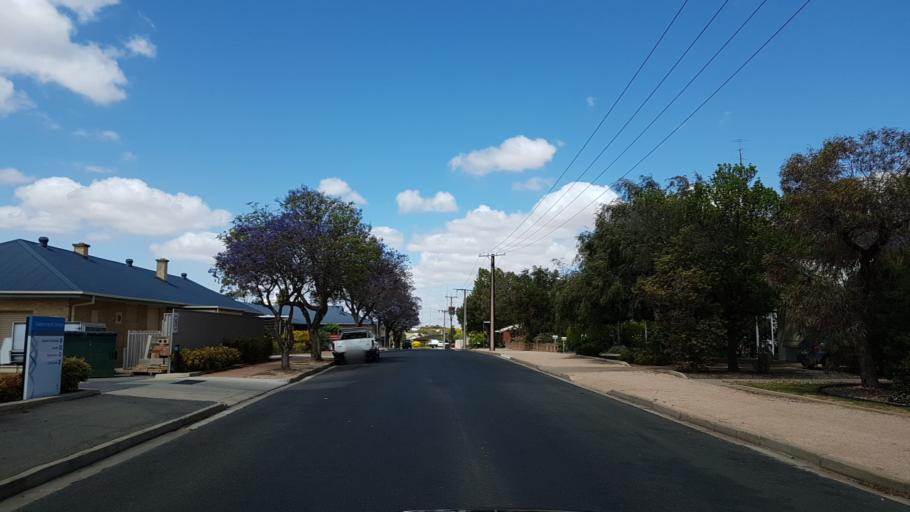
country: AU
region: South Australia
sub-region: Loxton Waikerie
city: Waikerie
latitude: -34.1828
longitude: 139.9845
